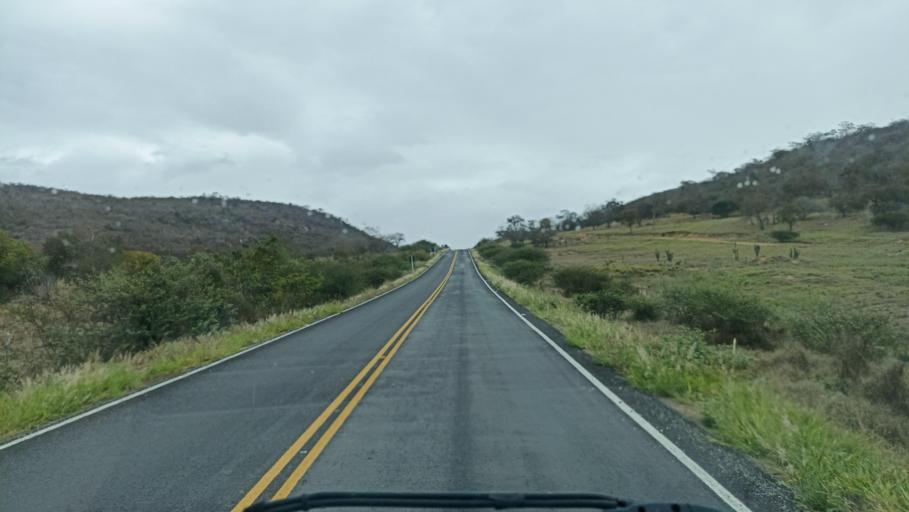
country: BR
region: Bahia
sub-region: Andarai
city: Vera Cruz
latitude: -13.0455
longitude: -40.7742
